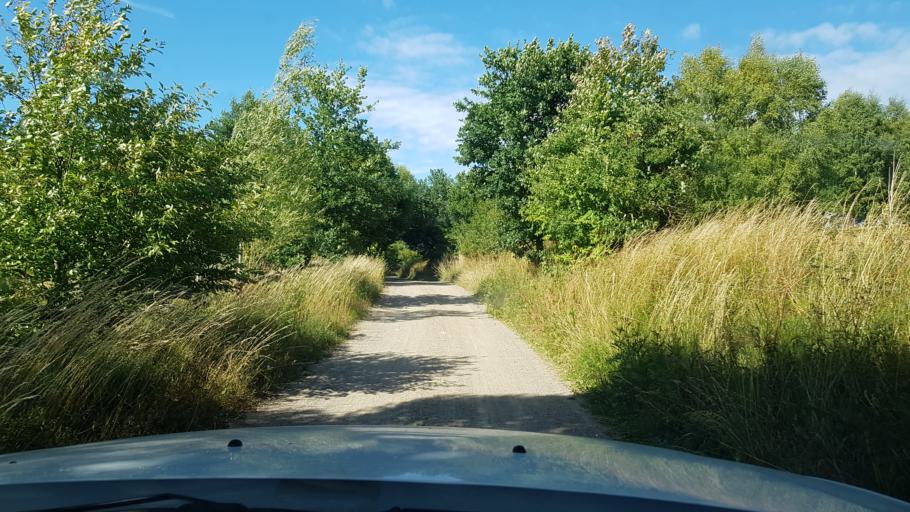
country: PL
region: West Pomeranian Voivodeship
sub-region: Powiat drawski
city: Zlocieniec
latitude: 53.6436
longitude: 16.0396
